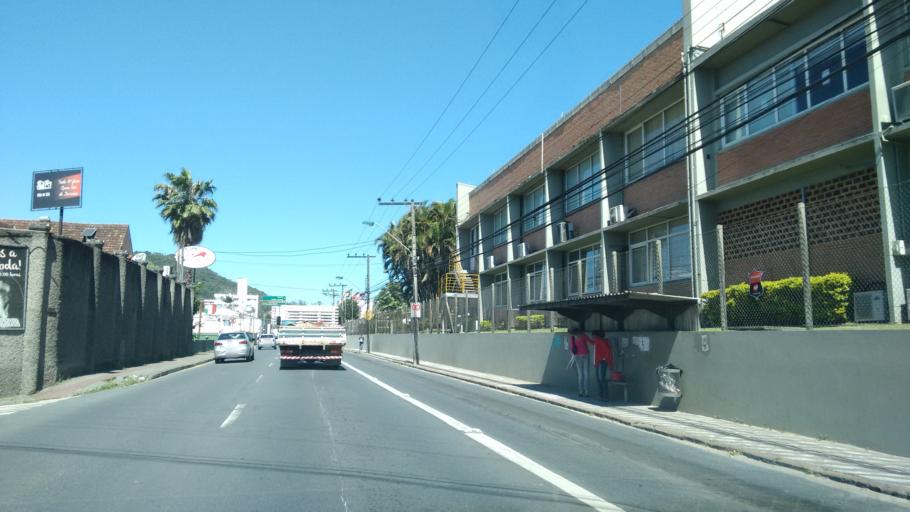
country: BR
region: Santa Catarina
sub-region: Blumenau
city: Blumenau
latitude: -26.8950
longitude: -49.0836
